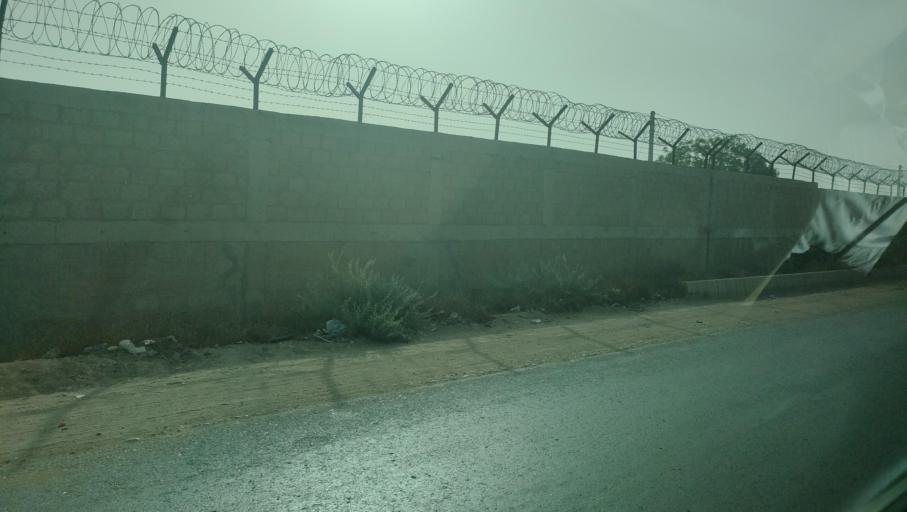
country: PK
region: Sindh
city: Malir Cantonment
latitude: 24.9210
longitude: 67.1858
